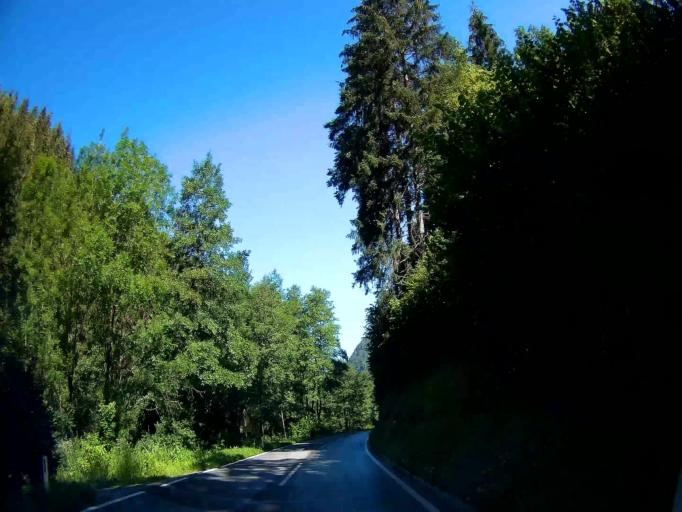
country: AT
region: Carinthia
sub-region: Politischer Bezirk Sankt Veit an der Glan
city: Bruckl
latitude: 46.7082
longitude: 14.5661
